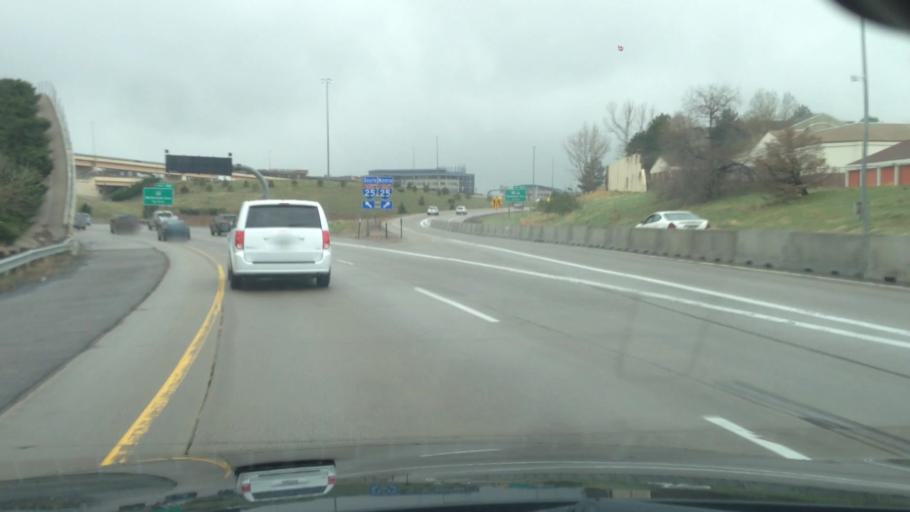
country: US
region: Colorado
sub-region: Arapahoe County
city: Castlewood
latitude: 39.6354
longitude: -104.9029
